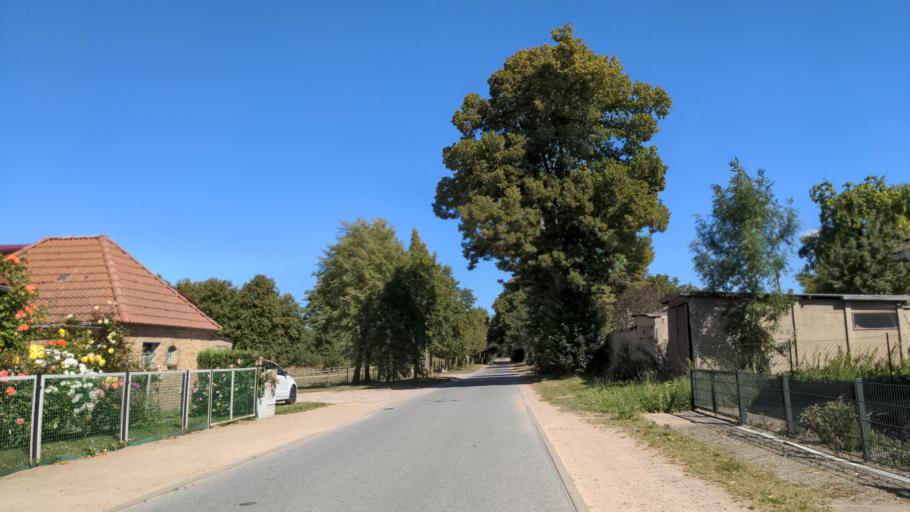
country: DE
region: Mecklenburg-Vorpommern
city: Ostseebad Boltenhagen
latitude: 53.9441
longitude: 11.2252
